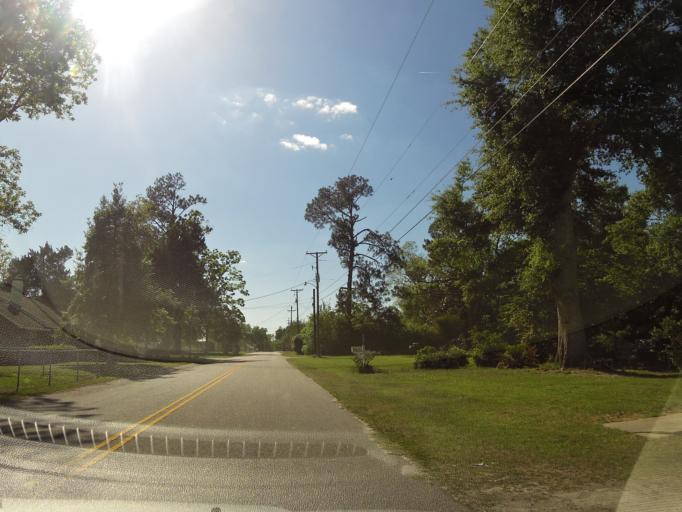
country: US
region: South Carolina
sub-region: Bamberg County
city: Denmark
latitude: 33.1794
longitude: -81.1829
